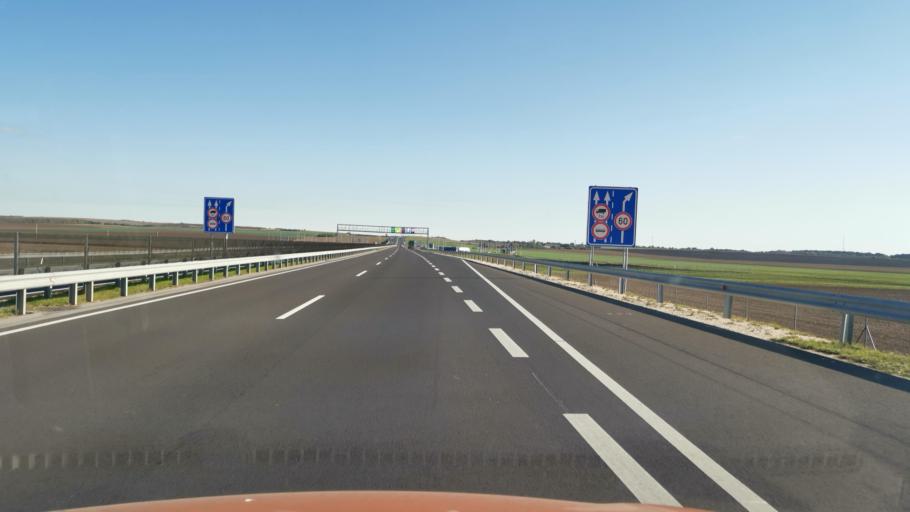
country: HU
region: Borsod-Abauj-Zemplen
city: Arnot
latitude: 48.1508
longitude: 20.8654
